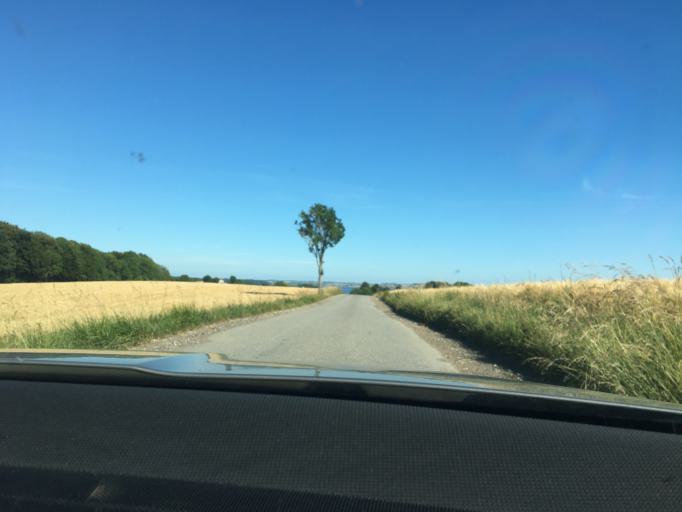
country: DK
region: Central Jutland
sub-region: Syddjurs Kommune
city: Hornslet
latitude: 56.2985
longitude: 10.3726
